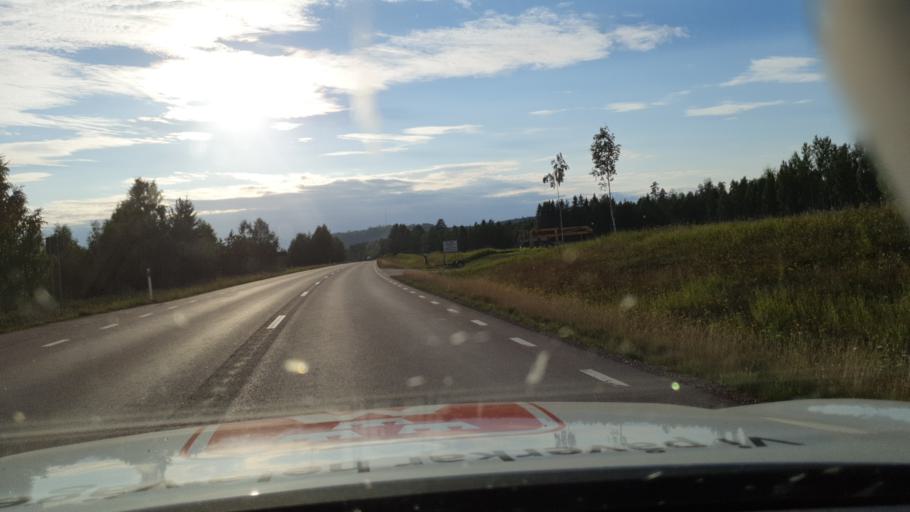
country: SE
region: Jaemtland
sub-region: Braecke Kommun
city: Braecke
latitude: 63.1653
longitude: 15.6532
